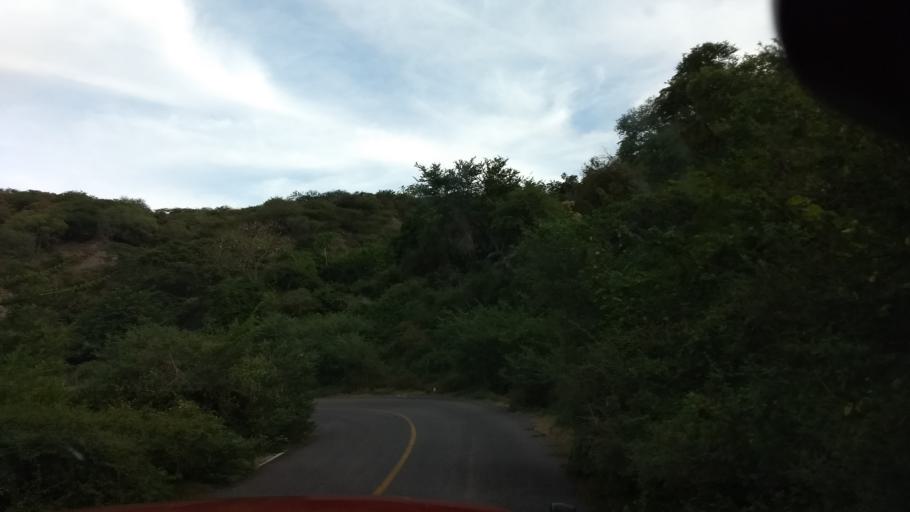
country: MX
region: Colima
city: Suchitlan
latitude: 19.4603
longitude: -103.8262
